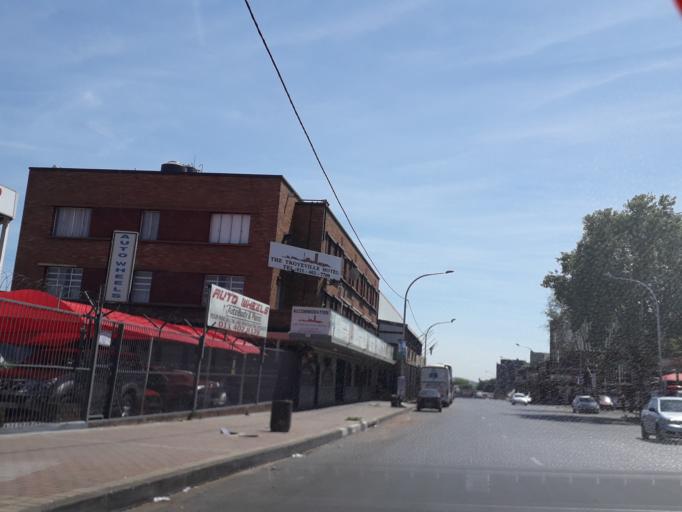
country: ZA
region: Gauteng
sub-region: City of Johannesburg Metropolitan Municipality
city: Johannesburg
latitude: -26.1993
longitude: 28.0659
